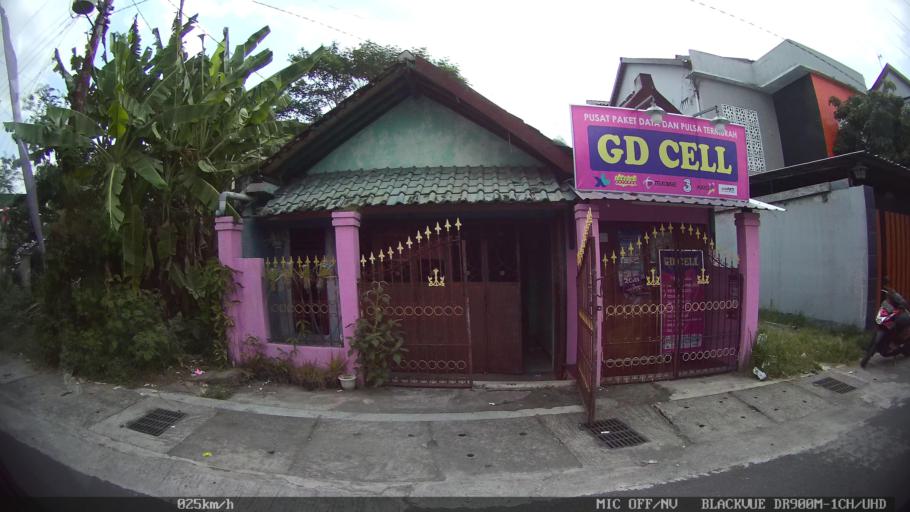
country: ID
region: Daerah Istimewa Yogyakarta
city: Gamping Lor
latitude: -7.8061
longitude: 110.3324
